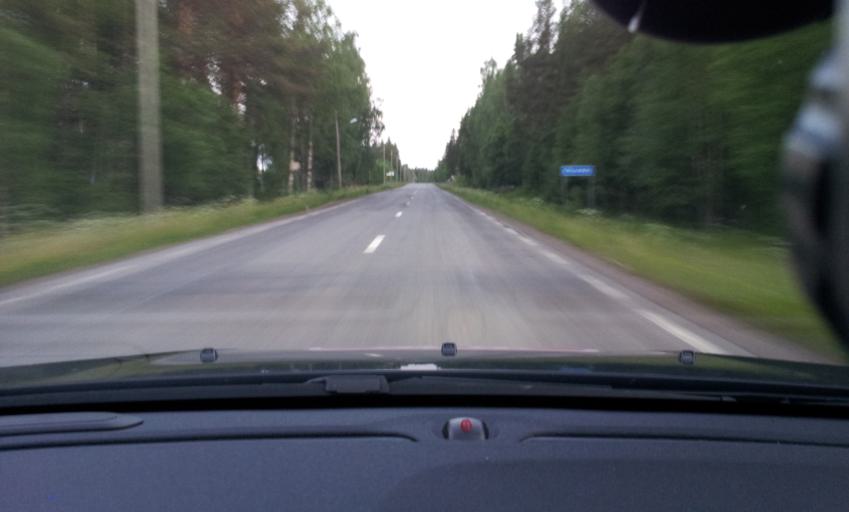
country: SE
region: Jaemtland
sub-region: Ragunda Kommun
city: Hammarstrand
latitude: 62.9902
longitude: 16.0938
